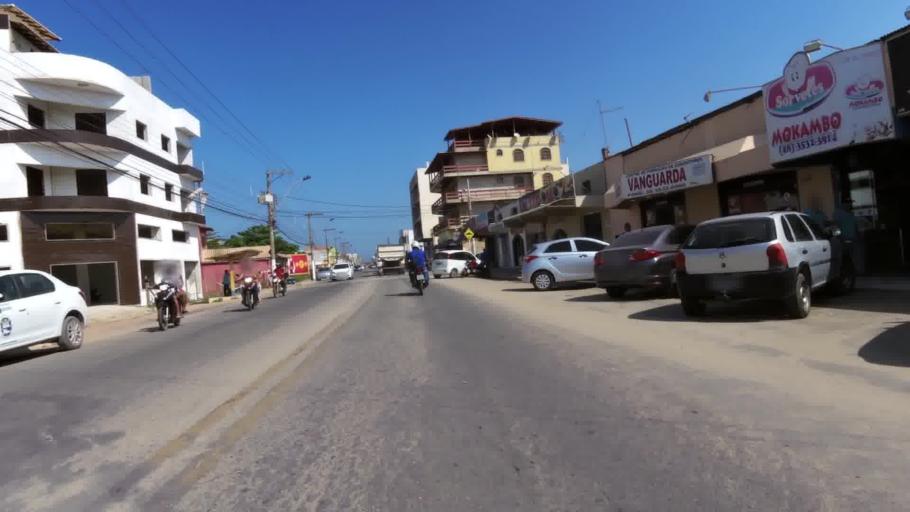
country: BR
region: Espirito Santo
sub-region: Itapemirim
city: Itapemirim
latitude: -21.0234
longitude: -40.8163
